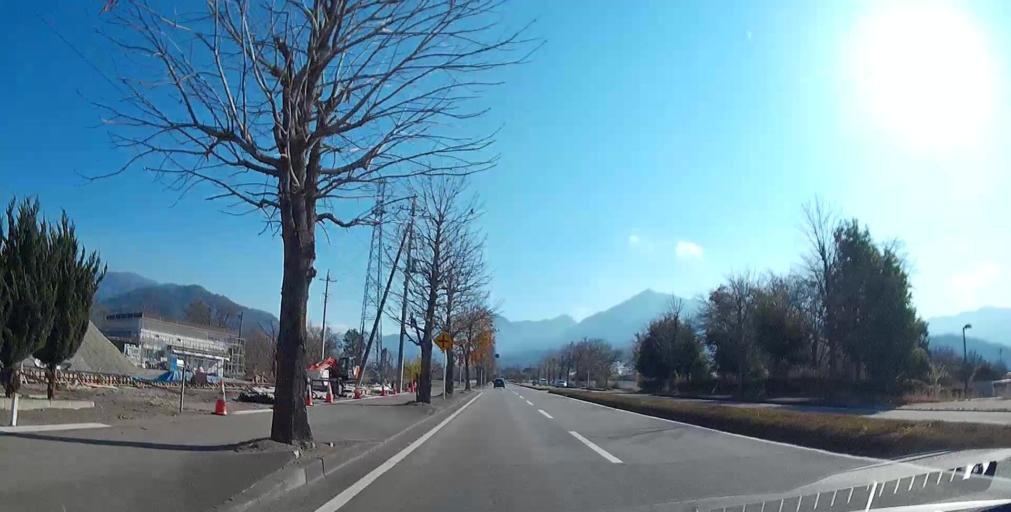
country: JP
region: Yamanashi
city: Isawa
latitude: 35.6263
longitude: 138.6849
